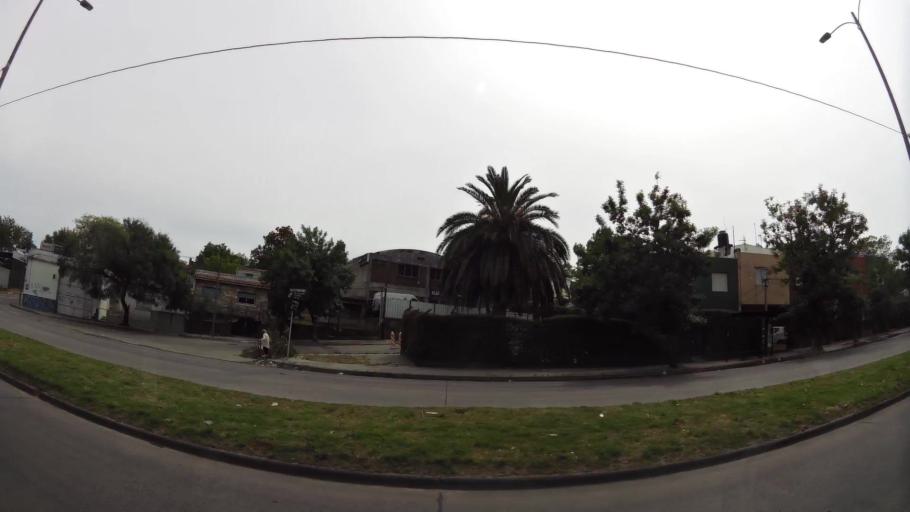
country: UY
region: Montevideo
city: Montevideo
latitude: -34.8599
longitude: -56.1734
